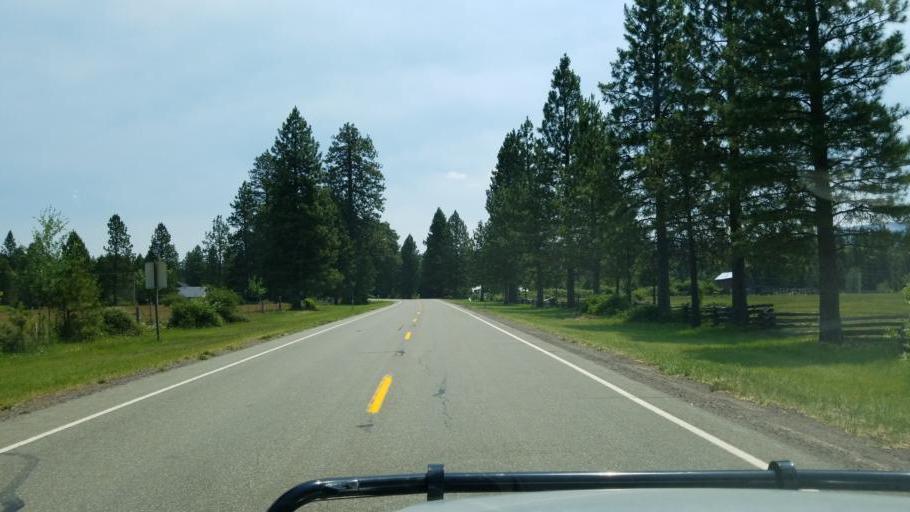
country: US
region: California
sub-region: Shasta County
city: Shingletown
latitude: 40.5172
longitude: -121.7029
